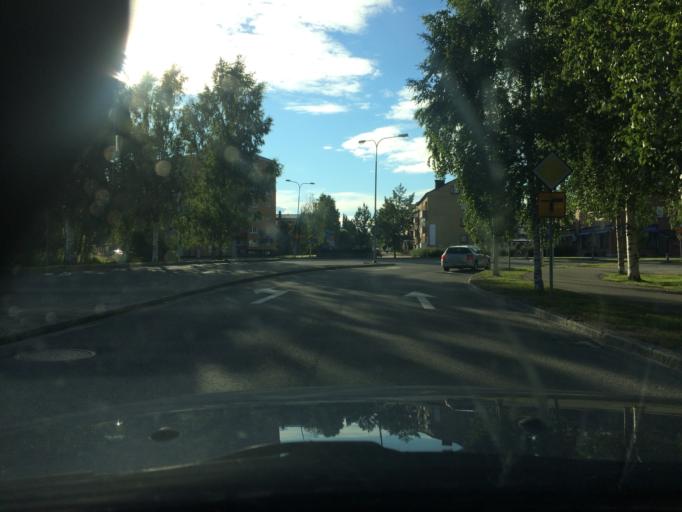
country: SE
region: Norrbotten
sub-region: Pitea Kommun
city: Pitea
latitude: 65.3189
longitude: 21.4735
